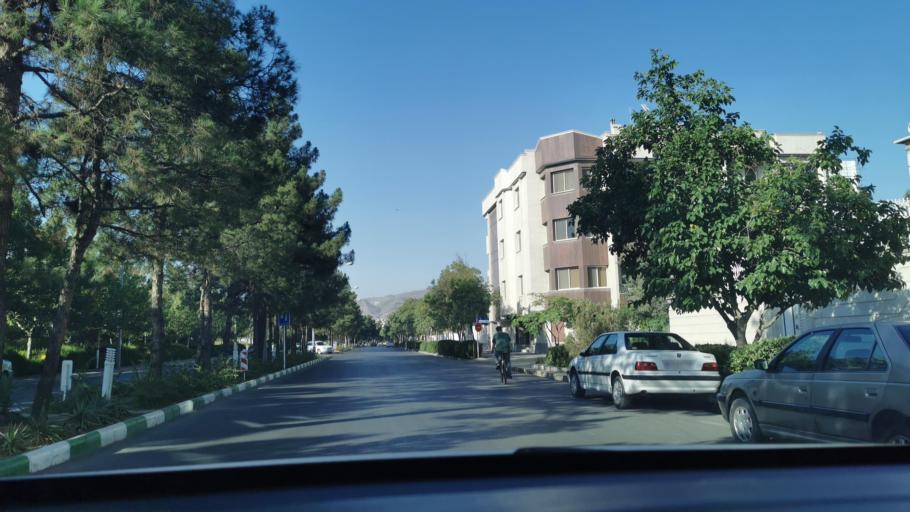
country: IR
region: Razavi Khorasan
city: Mashhad
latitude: 36.3183
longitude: 59.5272
